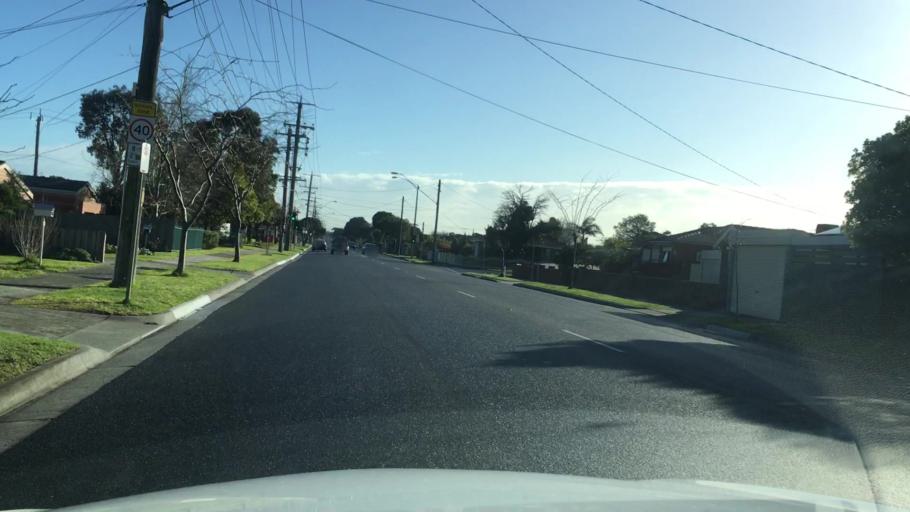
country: AU
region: Victoria
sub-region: Greater Dandenong
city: Keysborough
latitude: -37.9908
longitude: 145.1633
